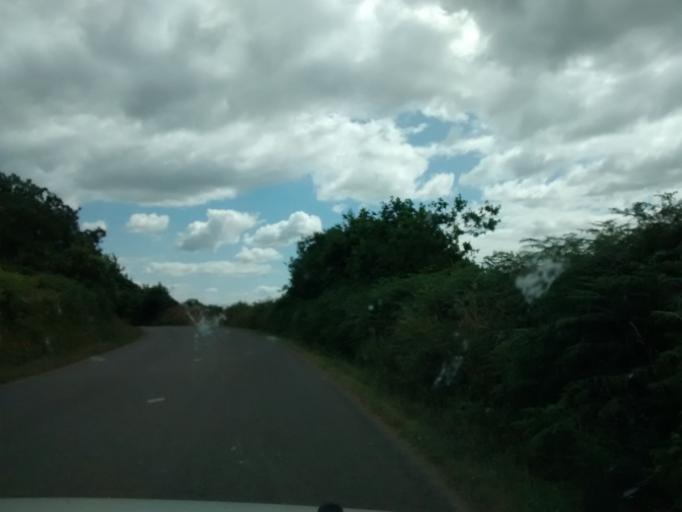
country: FR
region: Brittany
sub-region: Departement du Finistere
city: Plouider
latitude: 48.5916
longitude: -4.2890
